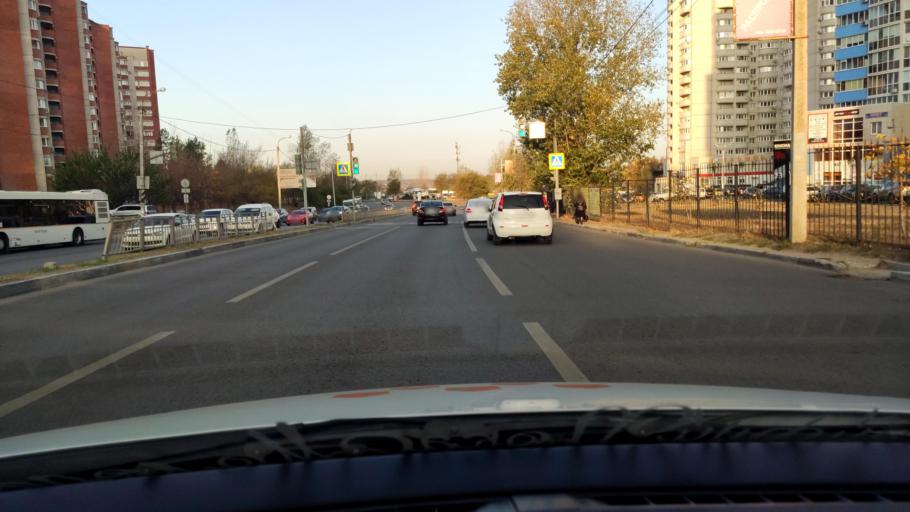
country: RU
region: Voronezj
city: Podgornoye
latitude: 51.7119
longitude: 39.1460
